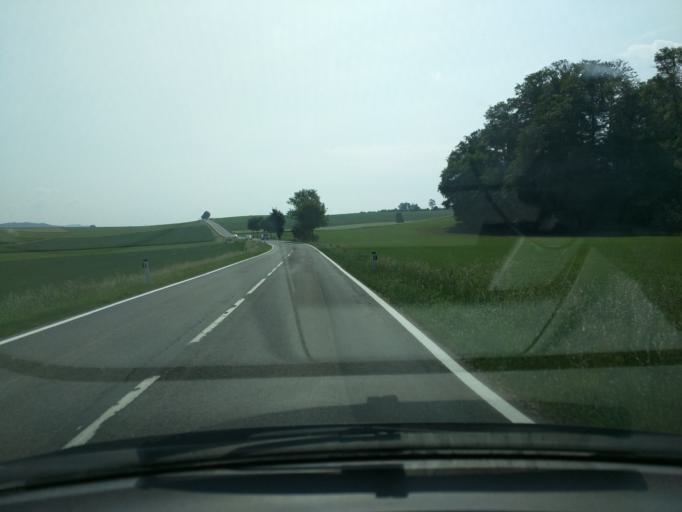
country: AT
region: Lower Austria
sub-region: Politischer Bezirk Scheibbs
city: Wieselburg
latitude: 48.1646
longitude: 15.1349
